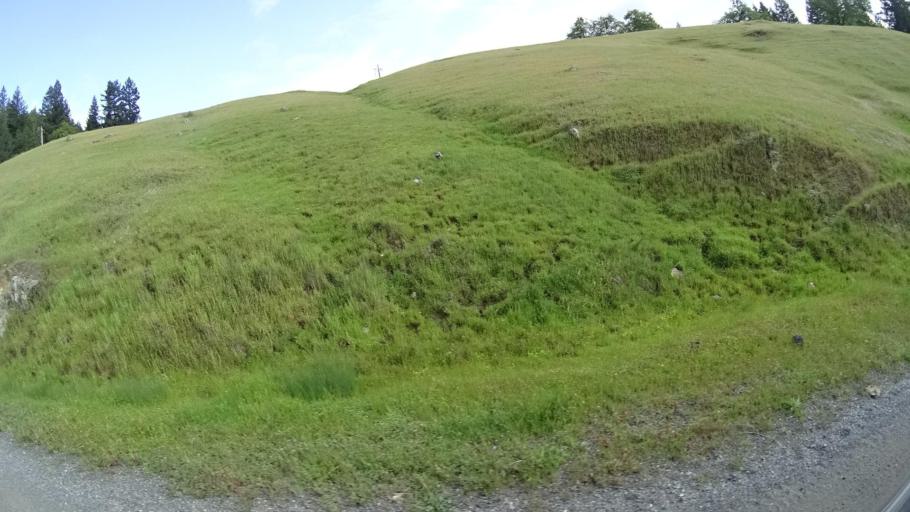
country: US
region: California
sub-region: Humboldt County
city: Redway
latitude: 40.2125
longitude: -123.6614
